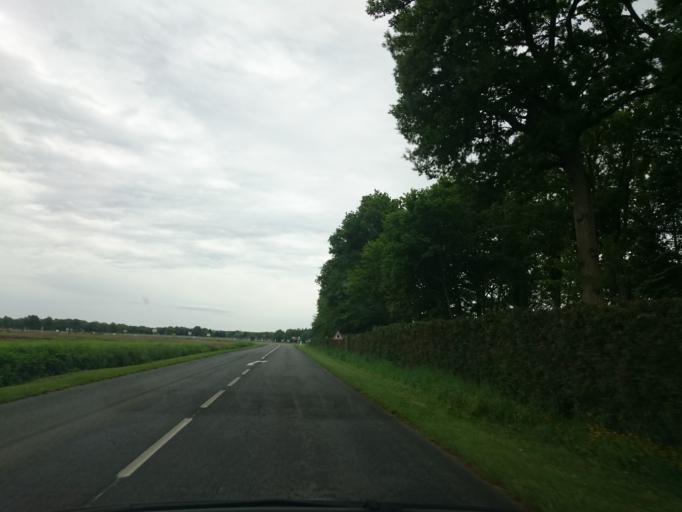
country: FR
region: Centre
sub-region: Departement du Loir-et-Cher
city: Muides-sur-Loire
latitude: 47.6642
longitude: 1.5339
